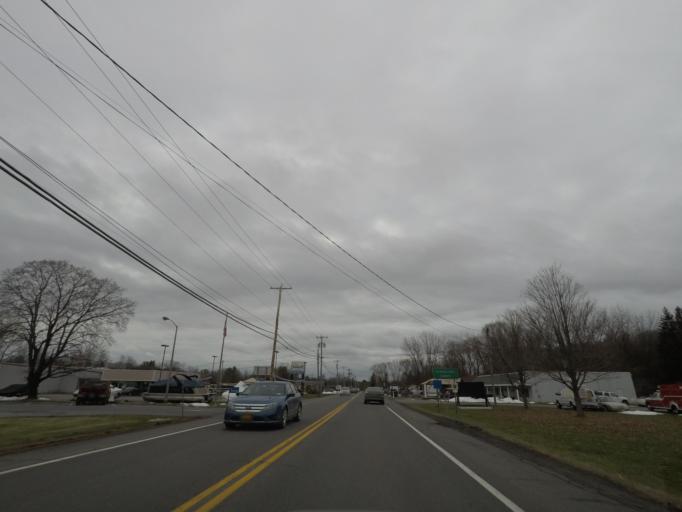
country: US
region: New York
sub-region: Schenectady County
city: East Glenville
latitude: 42.9047
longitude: -73.9030
